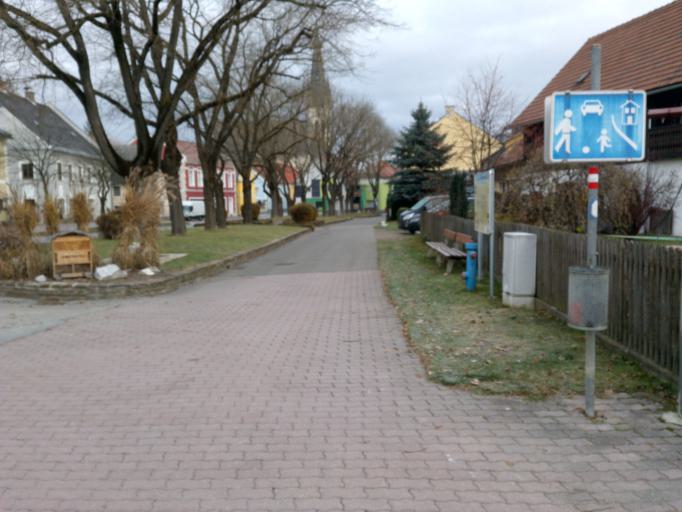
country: AT
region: Styria
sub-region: Politischer Bezirk Murtal
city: Weisskirchen in Steiermark
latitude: 47.1524
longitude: 14.7388
